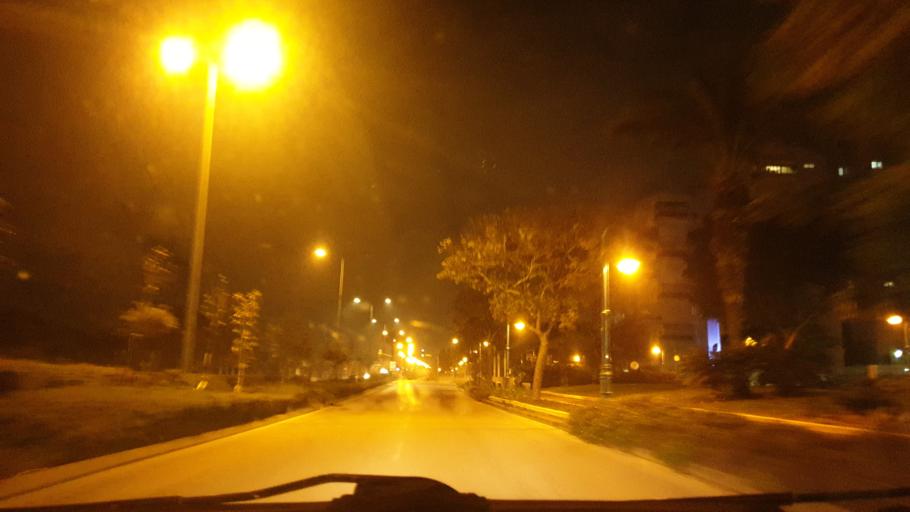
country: IL
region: Central District
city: Bet Dagan
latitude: 31.9744
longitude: 34.8157
